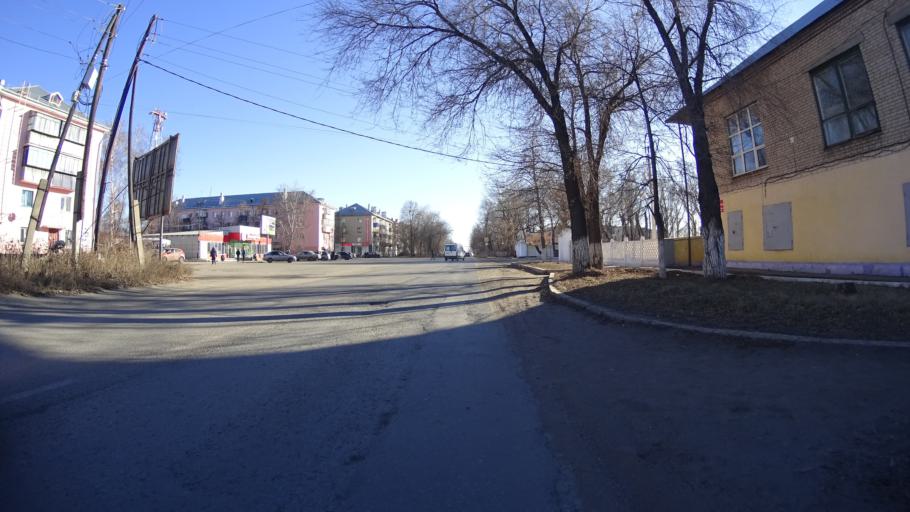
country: RU
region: Chelyabinsk
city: Troitsk
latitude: 54.1128
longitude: 61.5669
